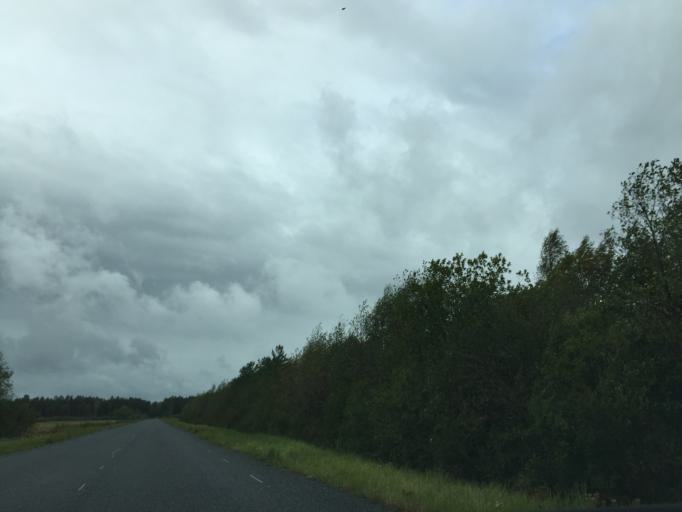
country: LV
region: Salacgrivas
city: Ainazi
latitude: 57.9713
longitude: 24.4277
